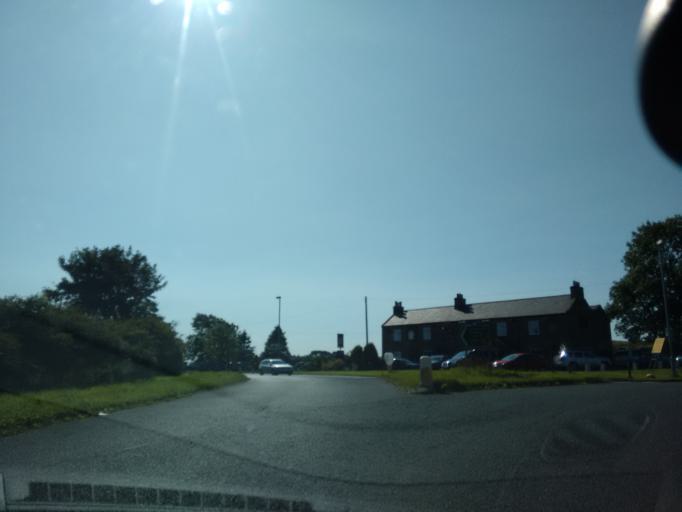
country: GB
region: England
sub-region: Northumberland
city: Corbridge
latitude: 55.0129
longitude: -2.0204
